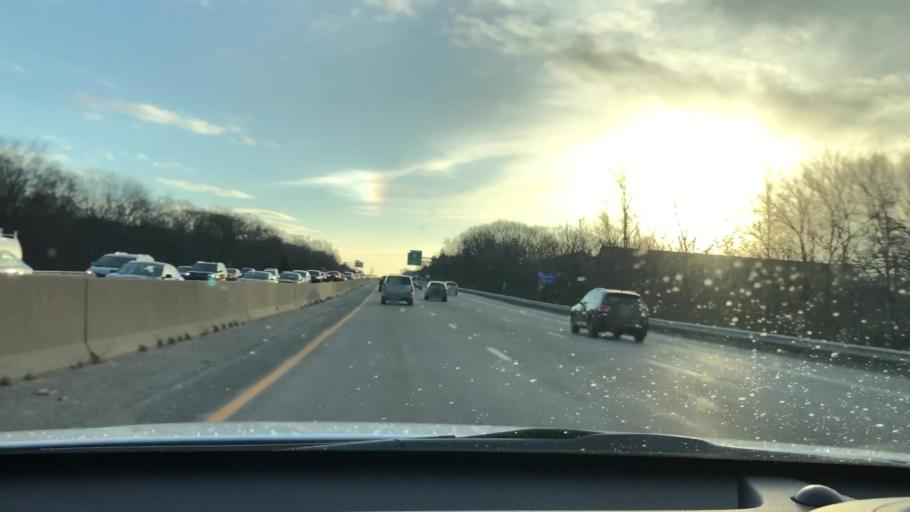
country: US
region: Massachusetts
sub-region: Norfolk County
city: Braintree
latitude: 42.2019
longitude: -70.9794
